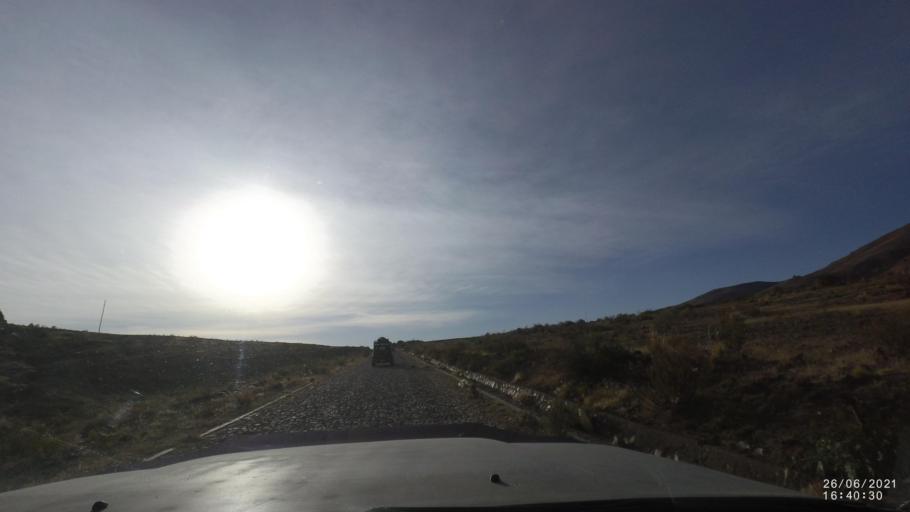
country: BO
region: Cochabamba
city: Arani
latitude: -17.7714
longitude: -65.8138
